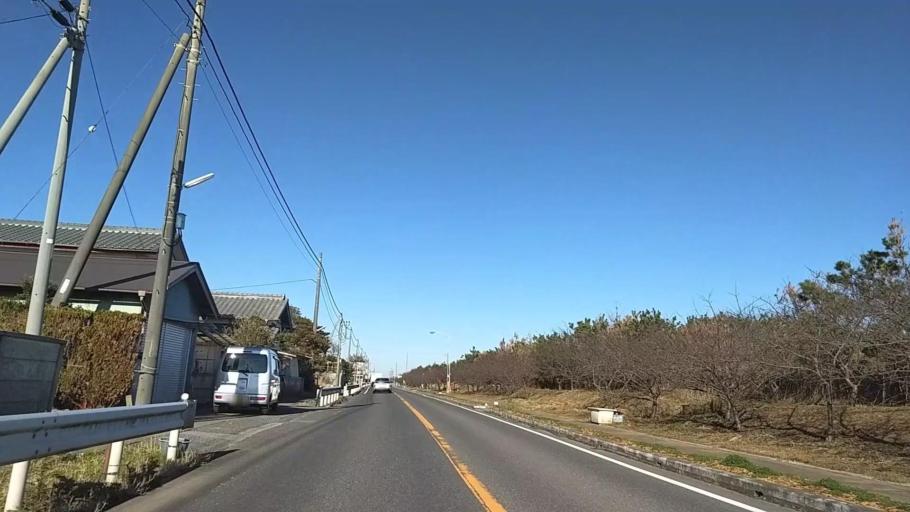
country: JP
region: Chiba
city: Togane
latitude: 35.4659
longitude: 140.4100
